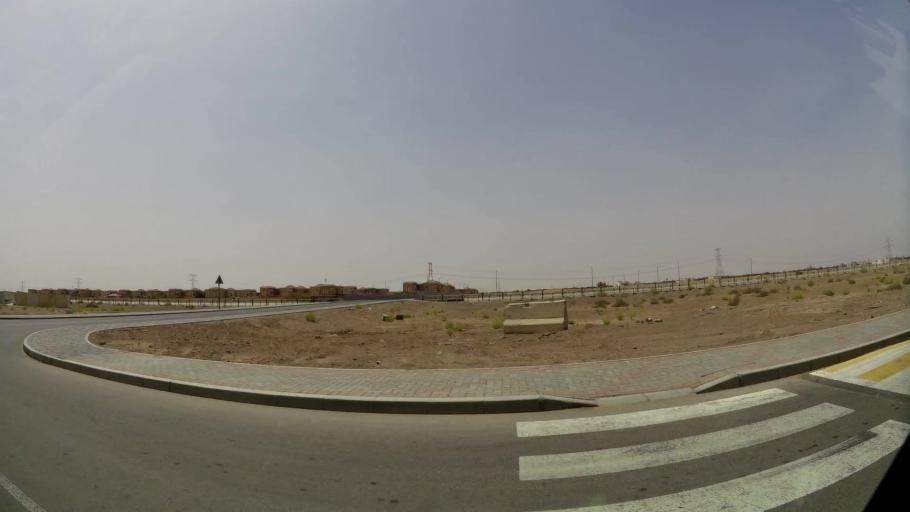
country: AE
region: Abu Dhabi
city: Al Ain
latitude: 24.1479
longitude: 55.6394
